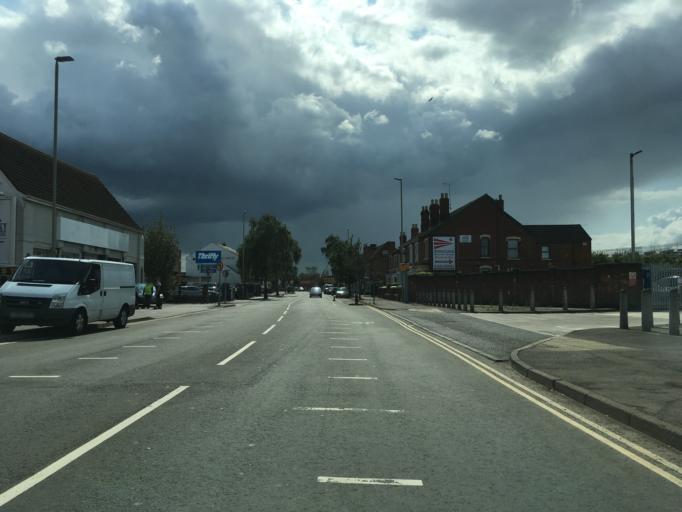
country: GB
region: England
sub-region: Gloucestershire
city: Gloucester
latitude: 51.8525
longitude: -2.2559
